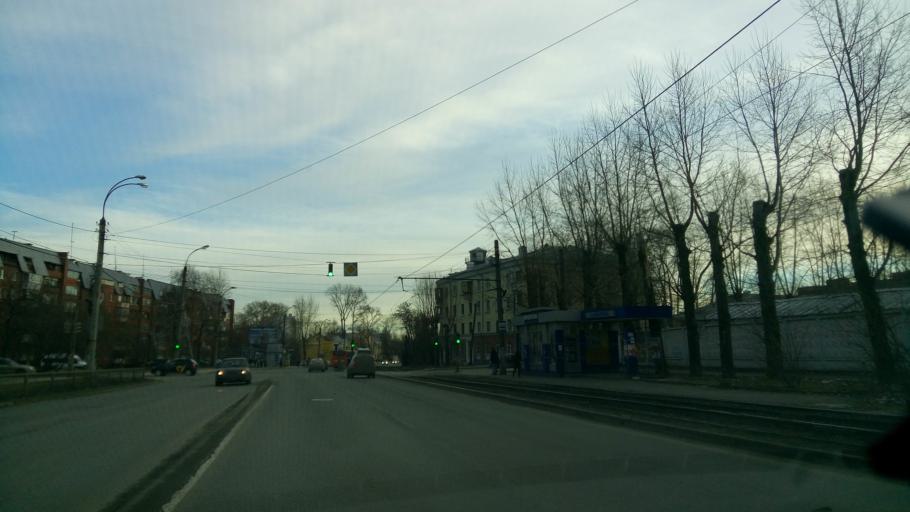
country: RU
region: Sverdlovsk
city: Shuvakish
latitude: 56.8745
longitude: 60.5173
